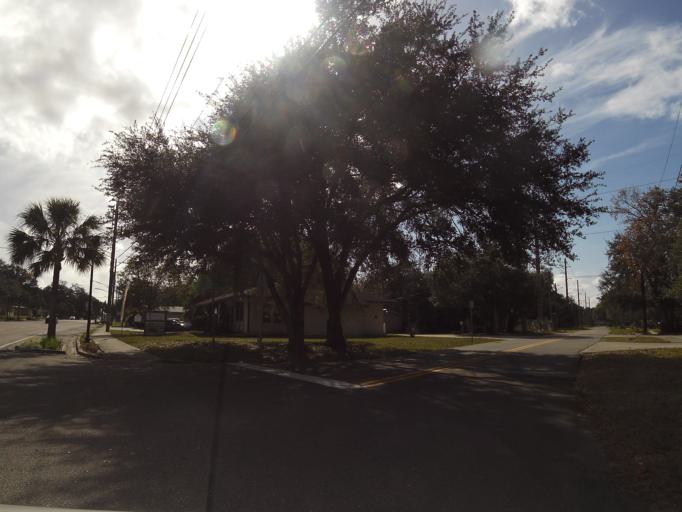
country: US
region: Florida
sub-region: Duval County
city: Jacksonville
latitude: 30.3408
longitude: -81.5893
